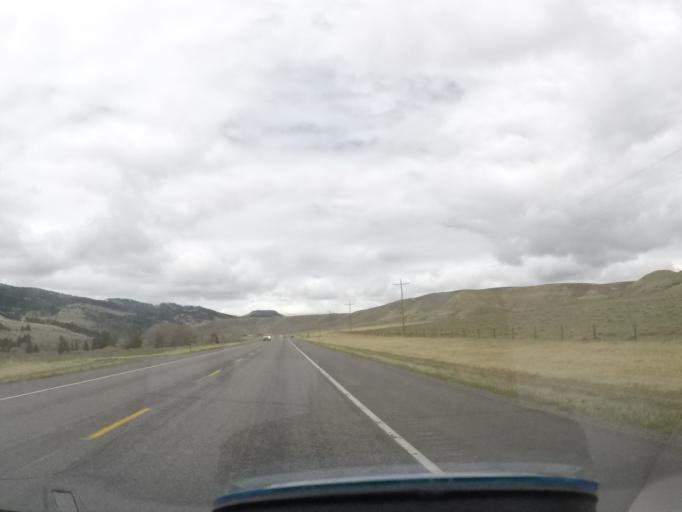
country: US
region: Wyoming
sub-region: Sublette County
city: Pinedale
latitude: 43.5751
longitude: -109.7319
